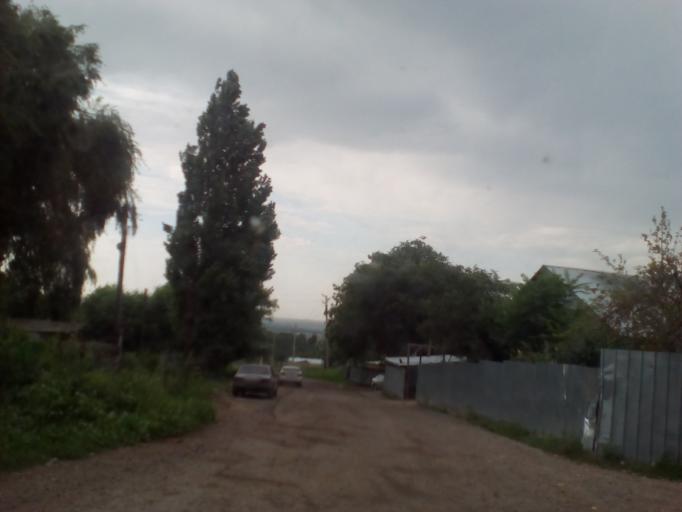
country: KZ
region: Almaty Oblysy
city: Burunday
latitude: 43.1536
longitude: 76.3852
